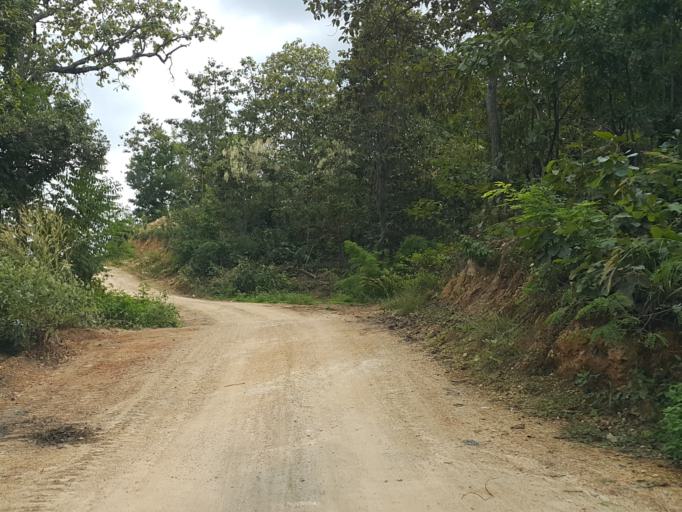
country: TH
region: Lampang
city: Chae Hom
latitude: 18.5709
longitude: 99.4425
